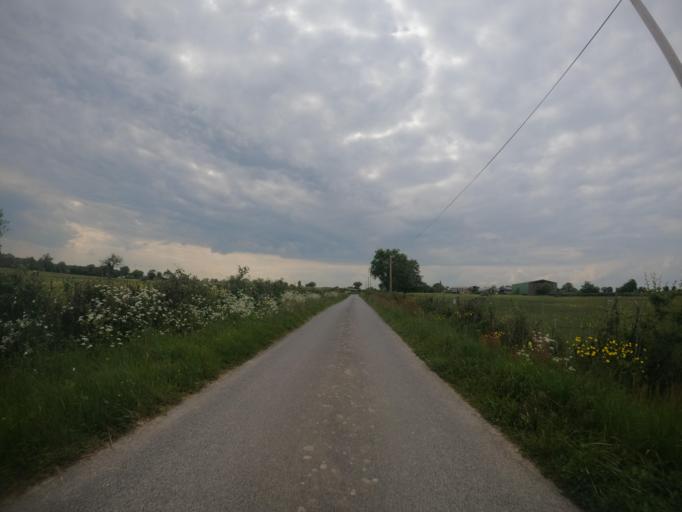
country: FR
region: Poitou-Charentes
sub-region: Departement des Deux-Sevres
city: Chiche
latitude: 46.8559
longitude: -0.3243
